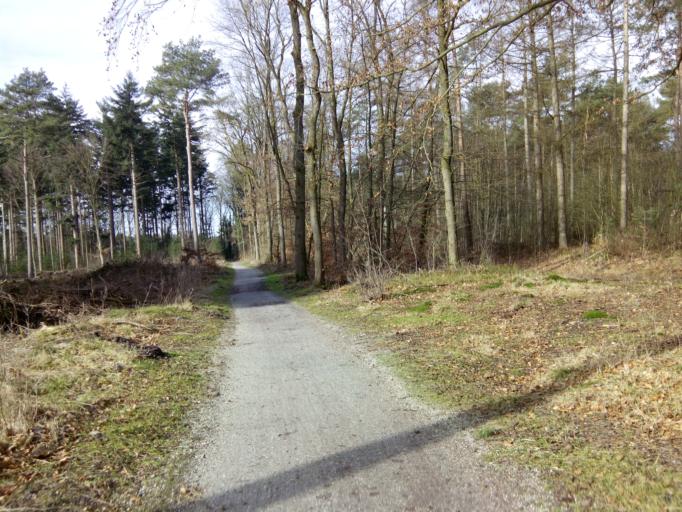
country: NL
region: Utrecht
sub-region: Gemeente Utrechtse Heuvelrug
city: Driebergen-Rijsenburg
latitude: 52.0772
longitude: 5.3223
